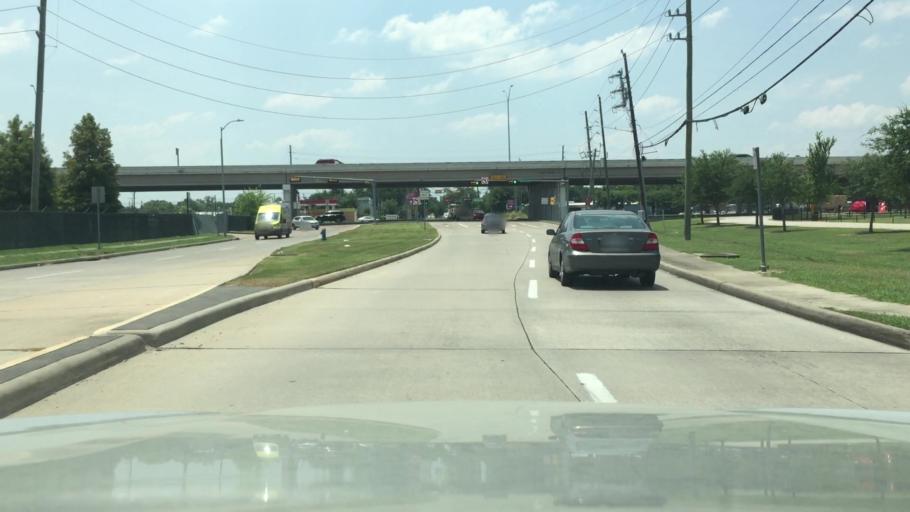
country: US
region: Texas
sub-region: Fort Bend County
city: Meadows Place
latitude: 29.7167
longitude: -95.5923
